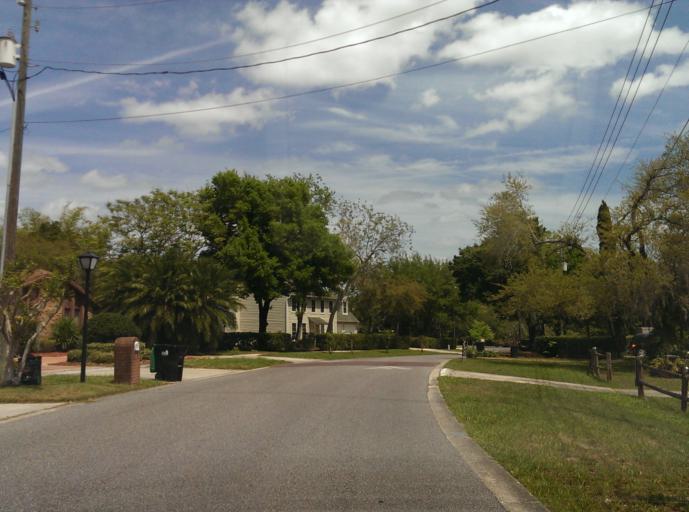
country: US
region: Florida
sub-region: Orange County
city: Doctor Phillips
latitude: 28.4785
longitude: -81.4876
